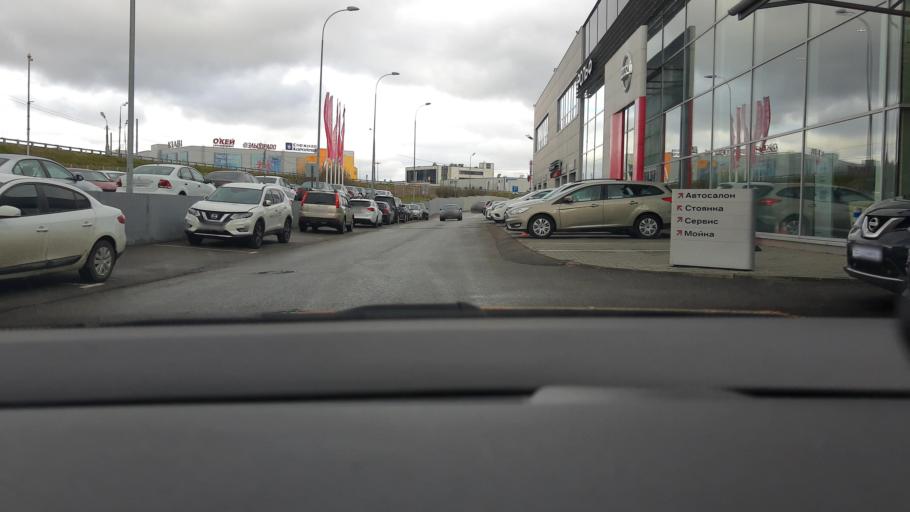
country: RU
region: Moscow
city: Lianozovo
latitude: 55.9108
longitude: 37.5920
